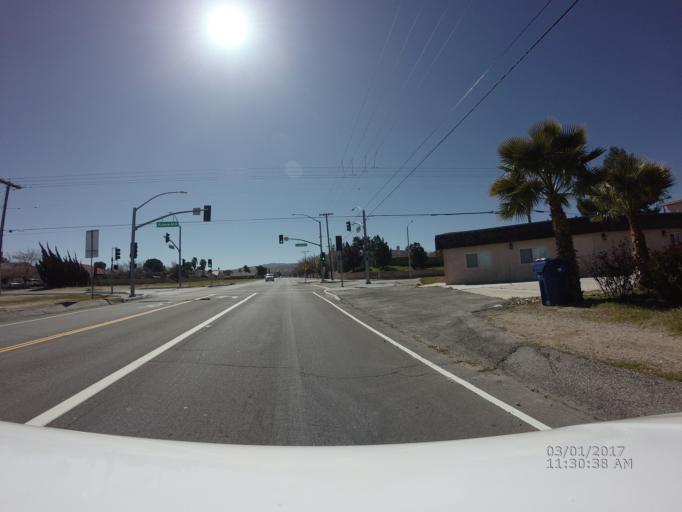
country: US
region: California
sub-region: Los Angeles County
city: Quartz Hill
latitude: 34.6385
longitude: -118.2187
